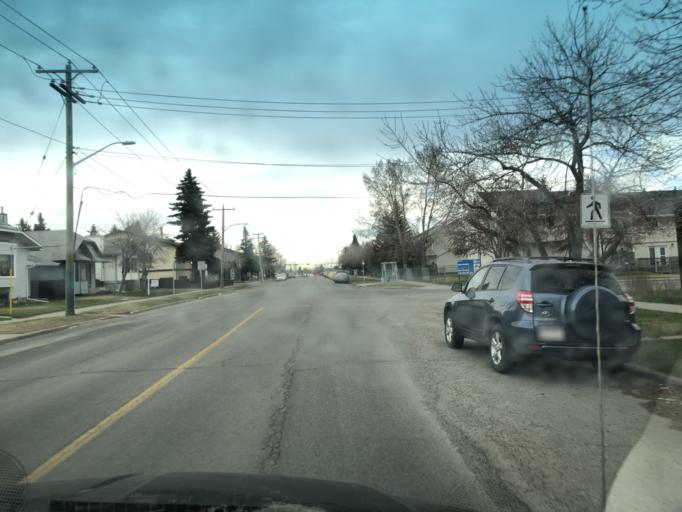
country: CA
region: Alberta
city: Calgary
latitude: 51.0715
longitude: -114.0134
